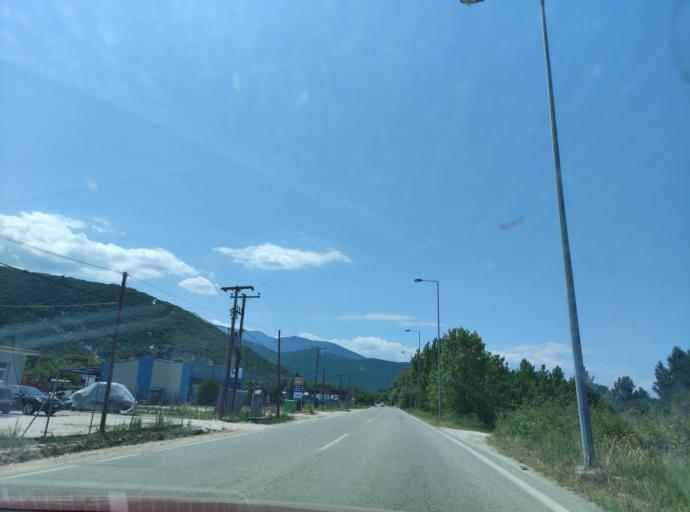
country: GR
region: East Macedonia and Thrace
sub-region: Nomos Kavalas
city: Palaiochori
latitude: 40.9514
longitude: 24.2038
